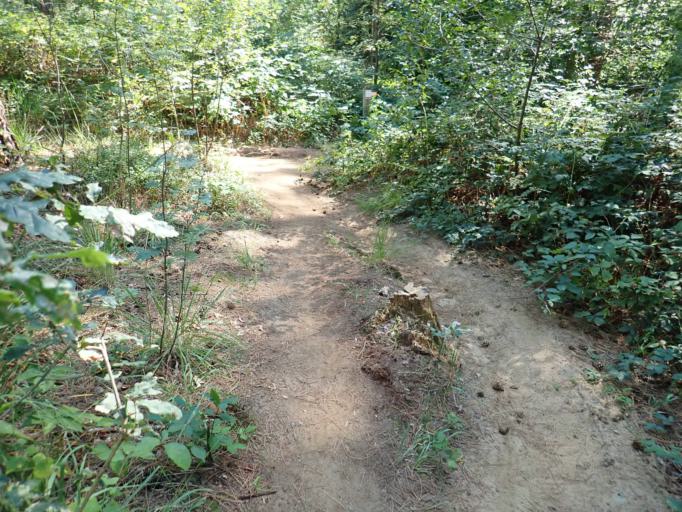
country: BE
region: Flanders
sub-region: Provincie Vlaams-Brabant
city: Scherpenheuvel-Zichem
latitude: 51.0264
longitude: 4.9653
